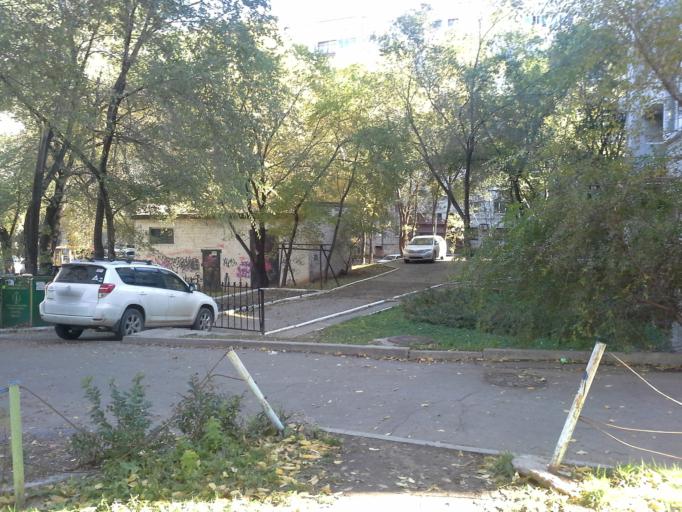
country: RU
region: Khabarovsk Krai
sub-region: Khabarovskiy Rayon
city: Khabarovsk
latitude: 48.4676
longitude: 135.0691
